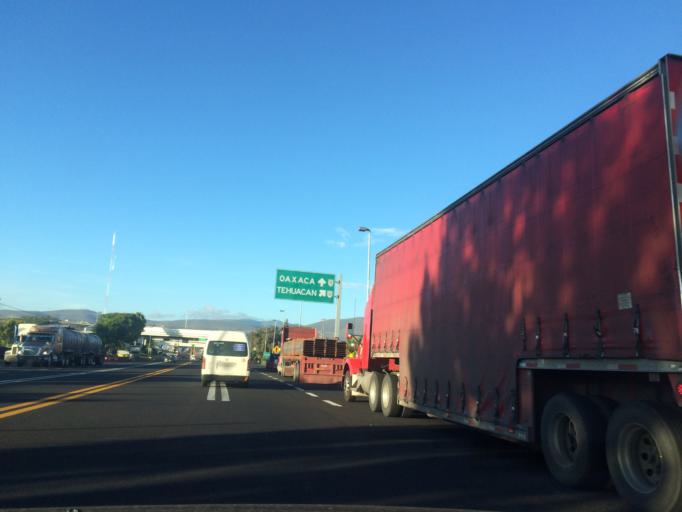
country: MX
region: Puebla
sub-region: Santiago Miahuatlan
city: San Jose Monte Chiquito
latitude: 18.4890
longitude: -97.4559
